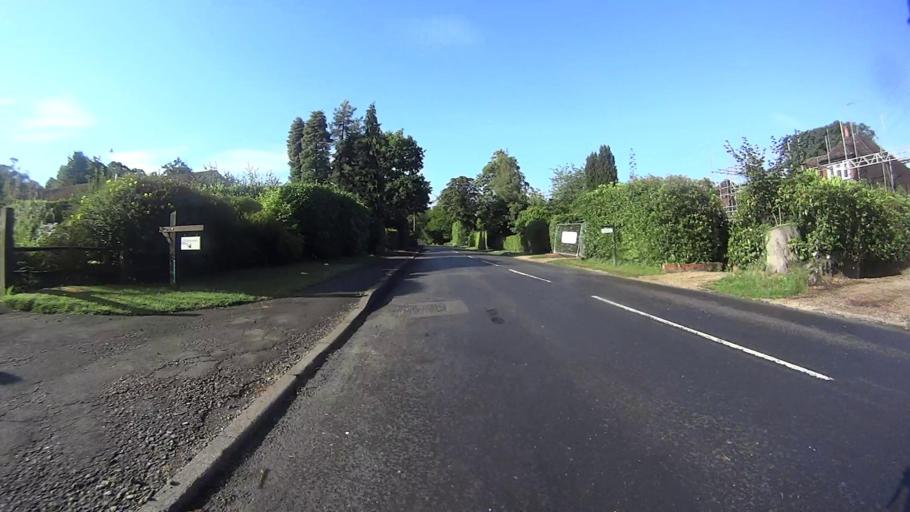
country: GB
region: England
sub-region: Surrey
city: Lingfield
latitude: 51.1553
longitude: -0.0235
